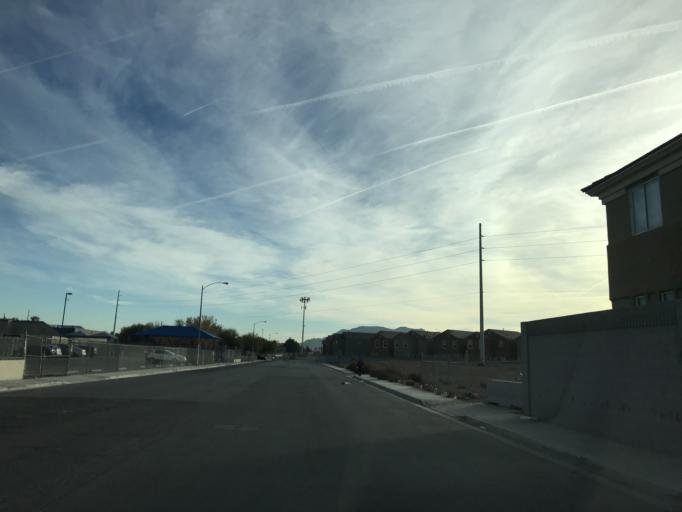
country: US
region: Nevada
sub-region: Clark County
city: Nellis Air Force Base
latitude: 36.2365
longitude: -115.0694
